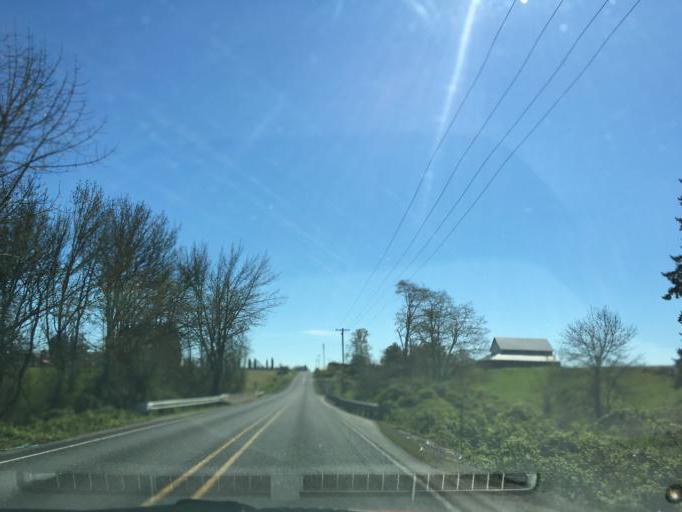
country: US
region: Oregon
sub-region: Clackamas County
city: Canby
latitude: 45.1937
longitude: -122.7227
